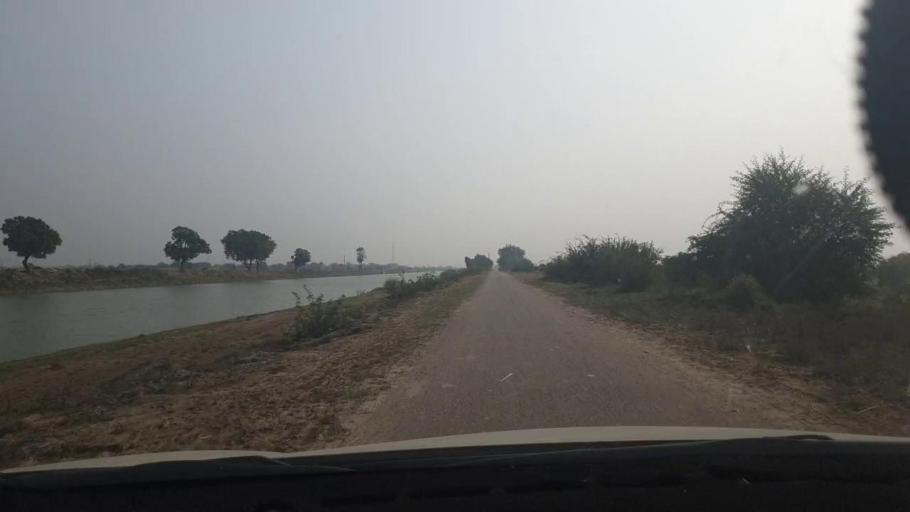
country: PK
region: Sindh
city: Tando Muhammad Khan
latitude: 24.9718
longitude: 68.4936
